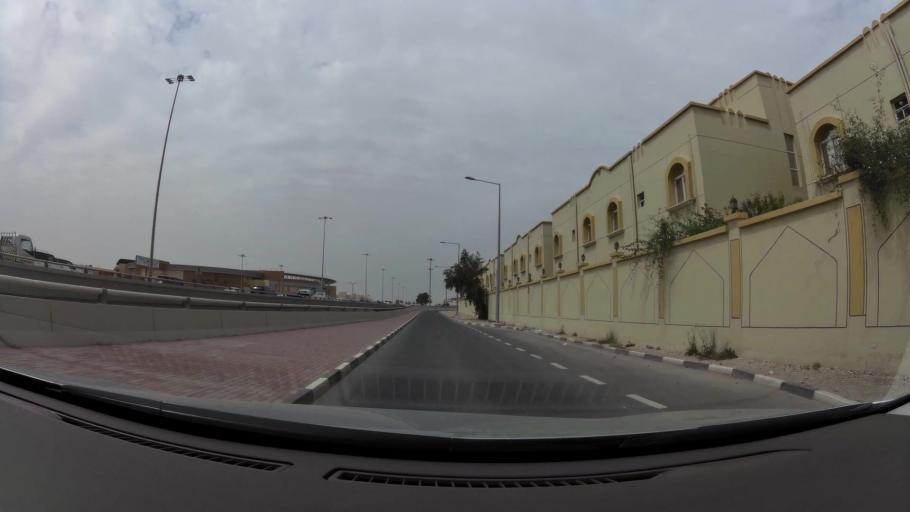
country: QA
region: Baladiyat ar Rayyan
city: Ar Rayyan
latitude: 25.3307
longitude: 51.4653
